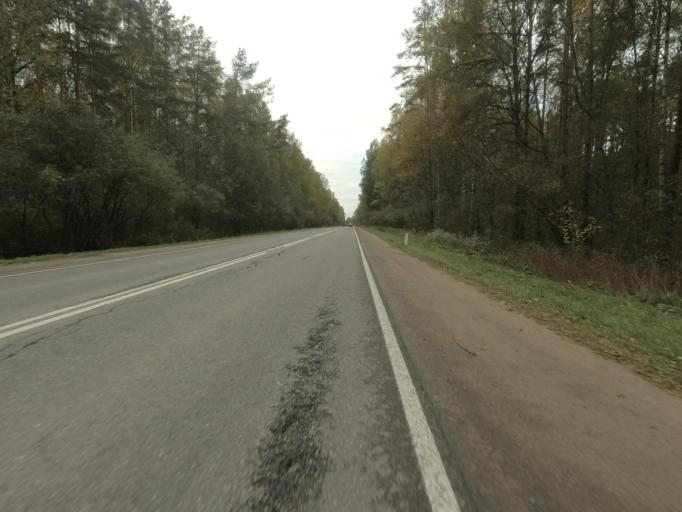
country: RU
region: Leningrad
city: Pavlovo
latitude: 59.8075
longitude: 30.9309
